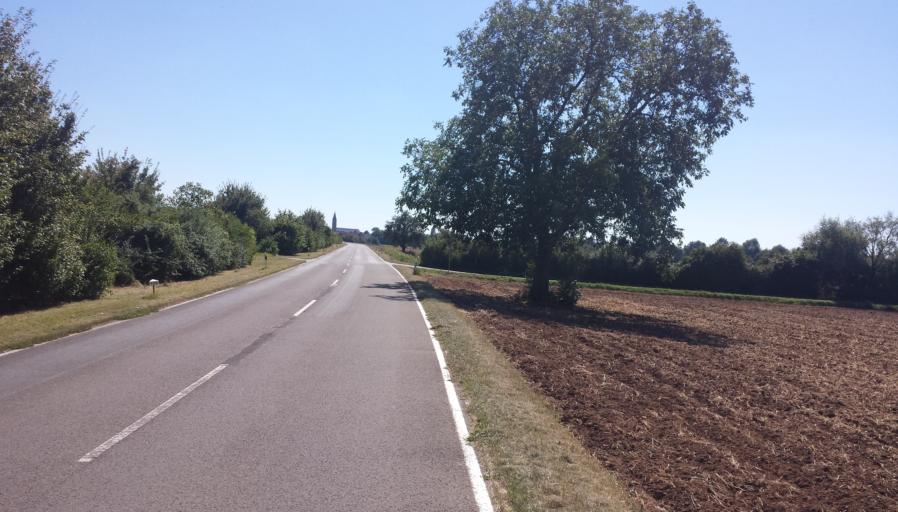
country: DE
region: Baden-Wuerttemberg
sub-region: Karlsruhe Region
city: Plankstadt
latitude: 49.4059
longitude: 8.5919
